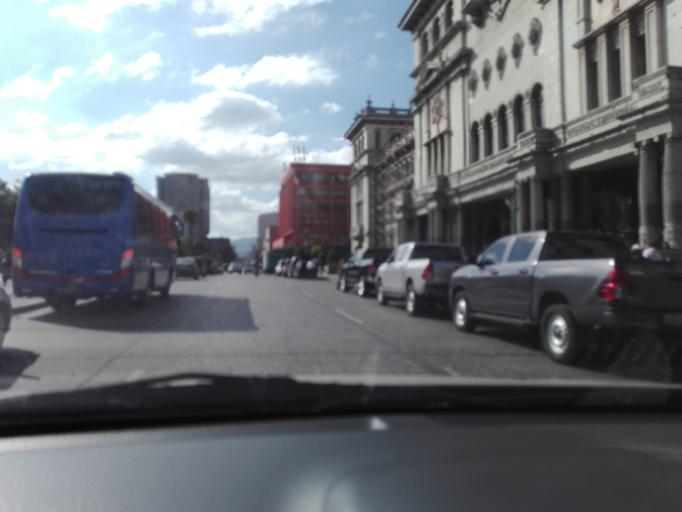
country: GT
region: Guatemala
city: Guatemala City
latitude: 14.6424
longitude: -90.5129
